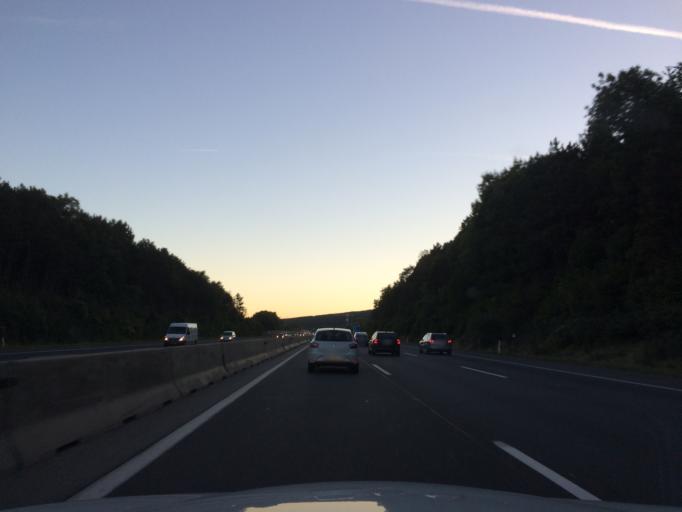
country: AT
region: Lower Austria
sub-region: Politischer Bezirk Wiener Neustadt
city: Theresienfeld
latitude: 47.8718
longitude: 16.1964
